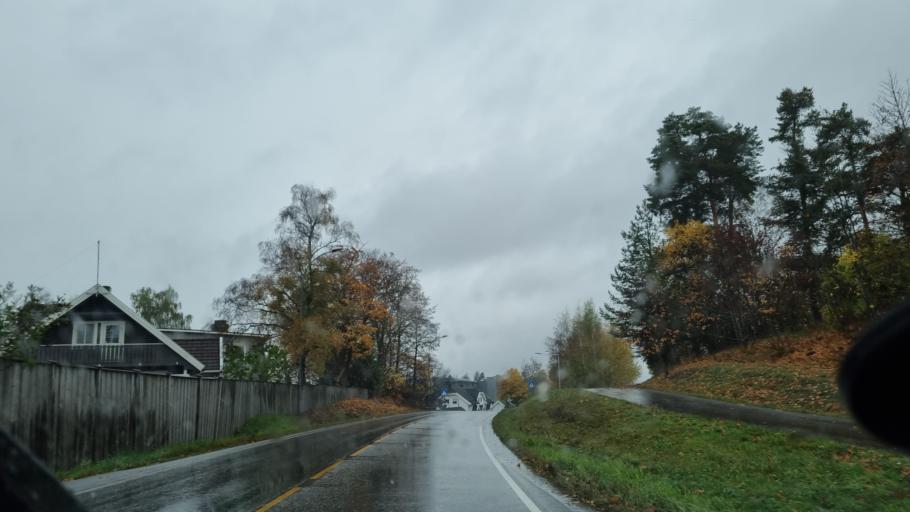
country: NO
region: Hedmark
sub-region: Hamar
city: Hamar
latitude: 60.8055
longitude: 11.1255
